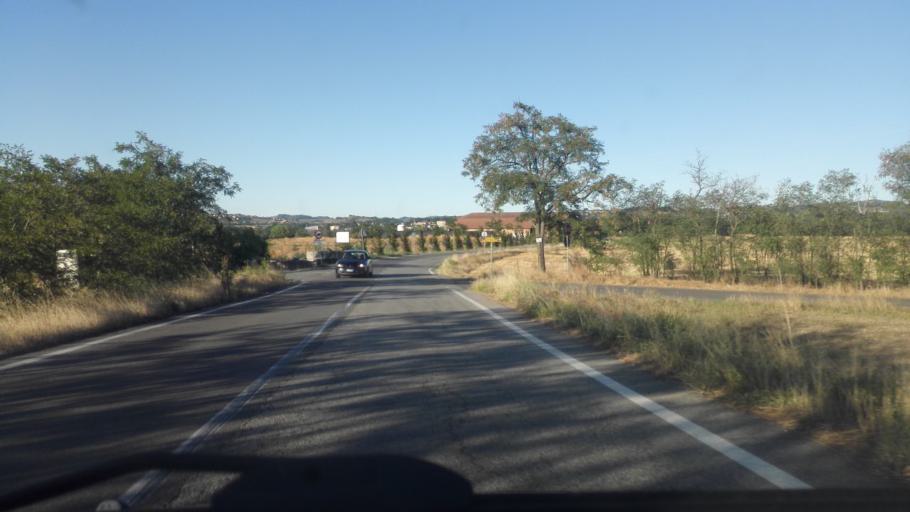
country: IT
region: Piedmont
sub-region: Provincia di Alessandria
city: Villalvernia
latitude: 44.8036
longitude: 8.8332
